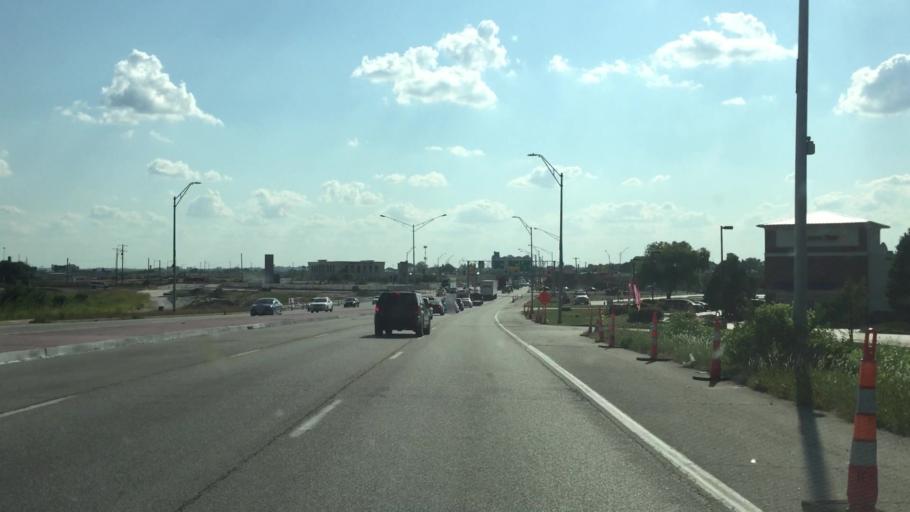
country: US
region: Missouri
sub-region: Clay County
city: North Kansas City
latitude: 39.1465
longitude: -94.5532
